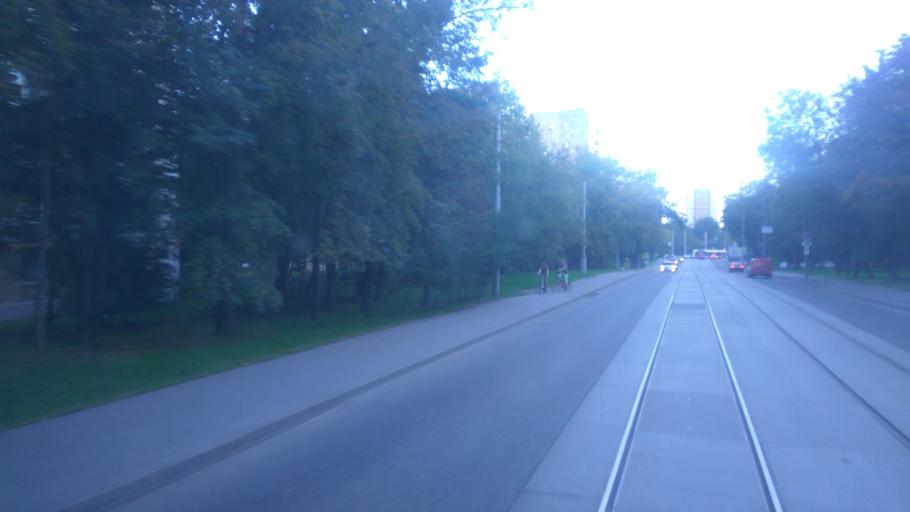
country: RU
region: Moskovskaya
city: Bogorodskoye
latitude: 55.8009
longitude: 37.7278
